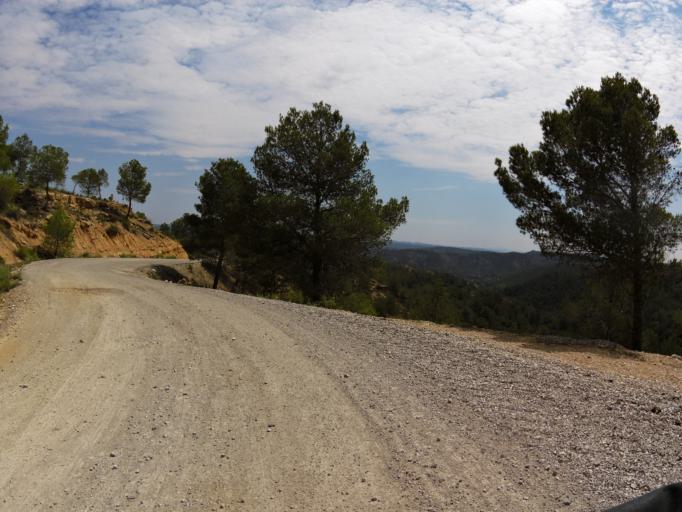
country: ES
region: Castille-La Mancha
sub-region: Provincia de Albacete
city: Casas Ibanez
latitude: 39.3627
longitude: -1.4667
